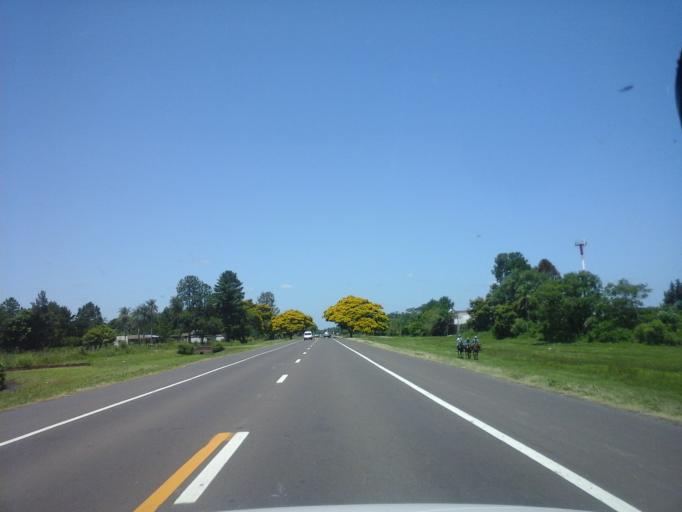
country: AR
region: Corrientes
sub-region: Departamento de San Cosme
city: San Cosme
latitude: -27.3768
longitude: -58.5010
